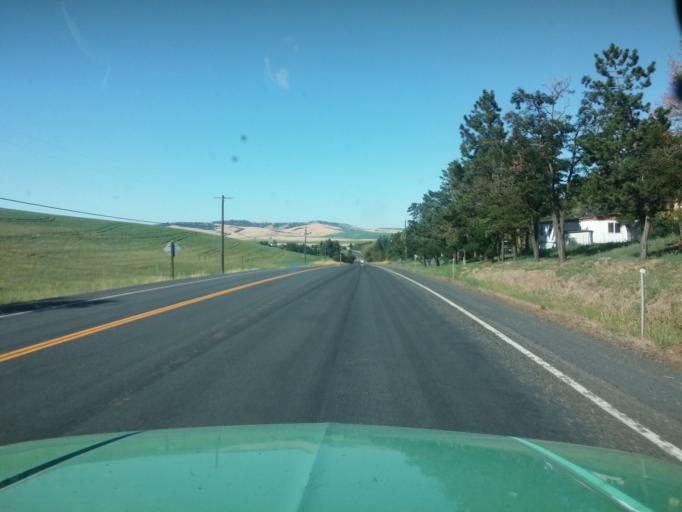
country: US
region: Idaho
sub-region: Latah County
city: Moscow
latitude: 46.6924
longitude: -117.0113
